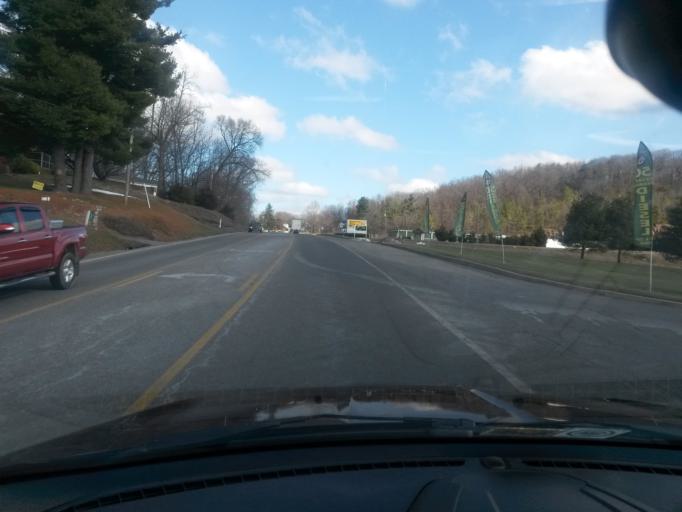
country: US
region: Virginia
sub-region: Augusta County
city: Jolivue
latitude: 38.1062
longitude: -79.0727
